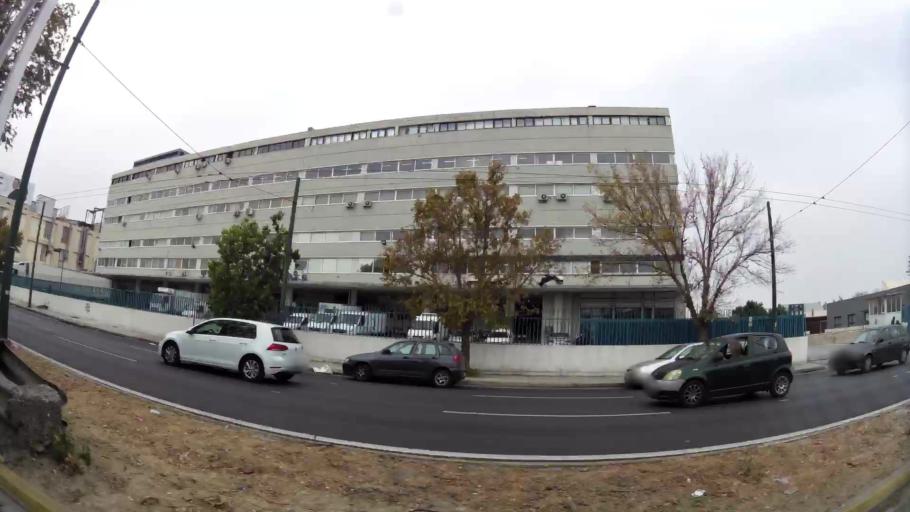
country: GR
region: Attica
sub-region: Nomarchia Athinas
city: Tavros
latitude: 37.9756
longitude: 23.6992
